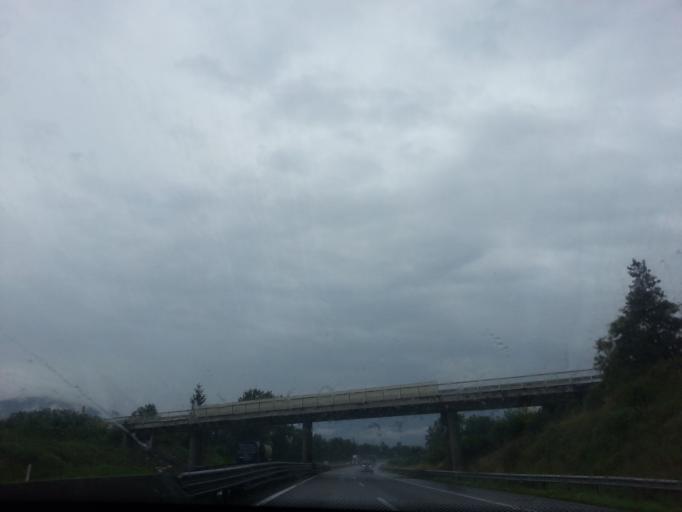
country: AT
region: Upper Austria
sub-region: Politischer Bezirk Kirchdorf an der Krems
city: Micheldorf in Oberoesterreich
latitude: 47.9537
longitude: 14.1015
